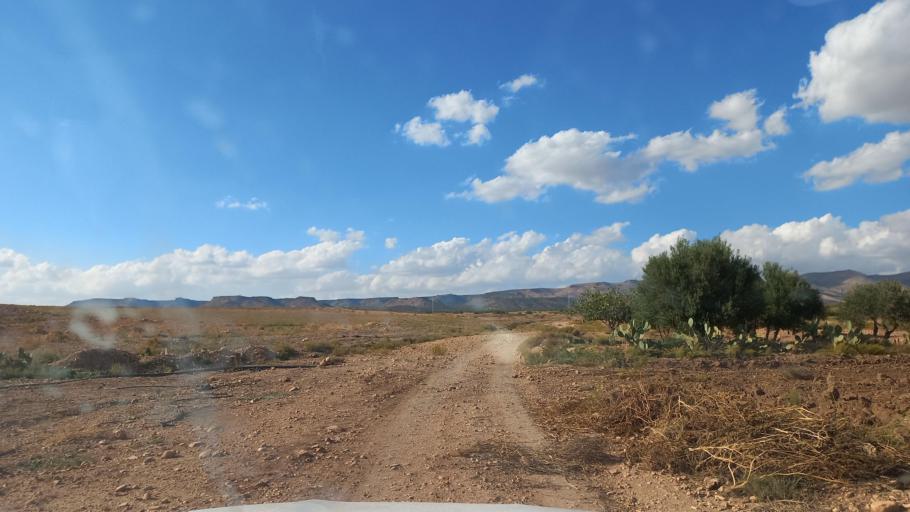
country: TN
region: Al Qasrayn
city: Sbiba
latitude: 35.3982
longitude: 9.0319
